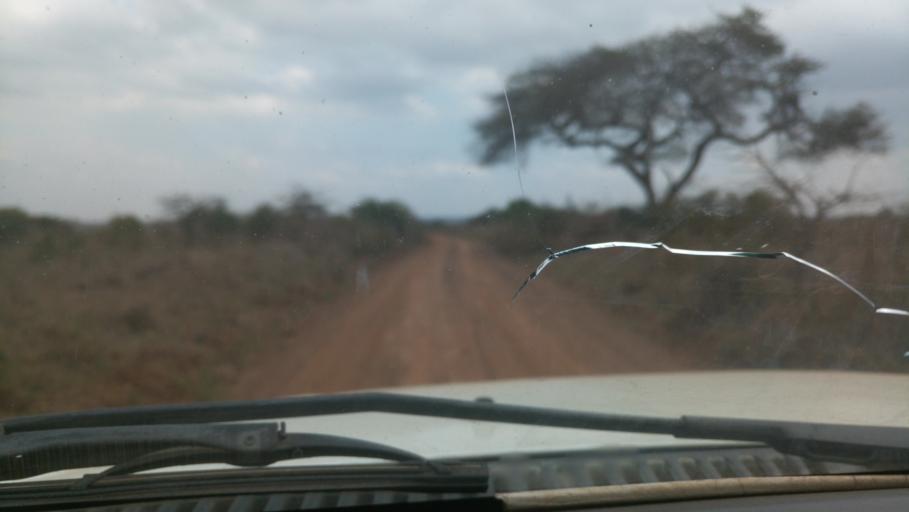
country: KE
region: Nairobi Area
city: Nairobi
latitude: -1.3649
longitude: 36.8325
